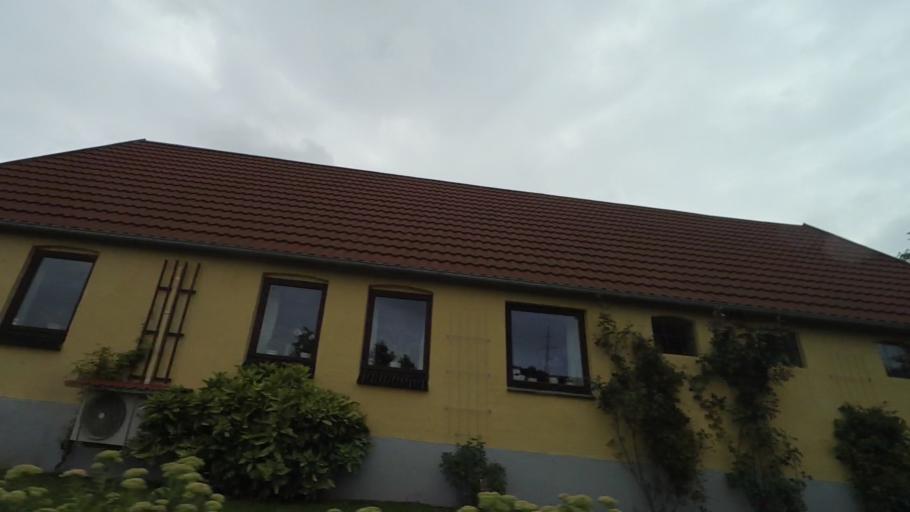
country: DK
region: Central Jutland
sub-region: Syddjurs Kommune
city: Ronde
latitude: 56.3328
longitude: 10.4570
